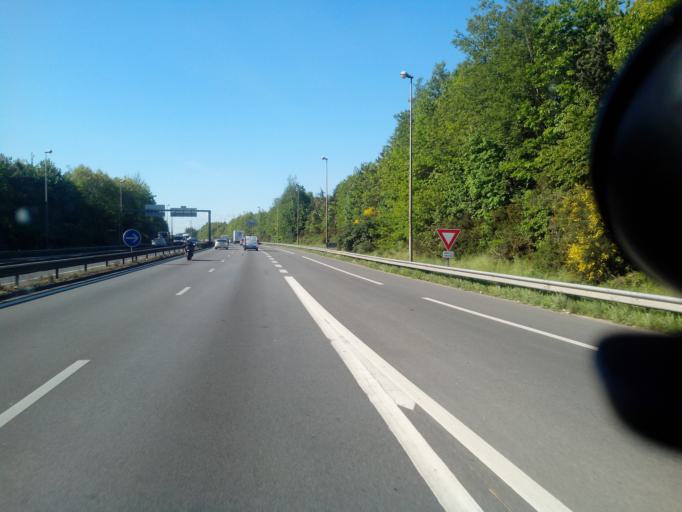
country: FR
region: Pays de la Loire
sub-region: Departement de la Loire-Atlantique
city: Saint-Herblain
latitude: 47.2182
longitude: -1.6242
